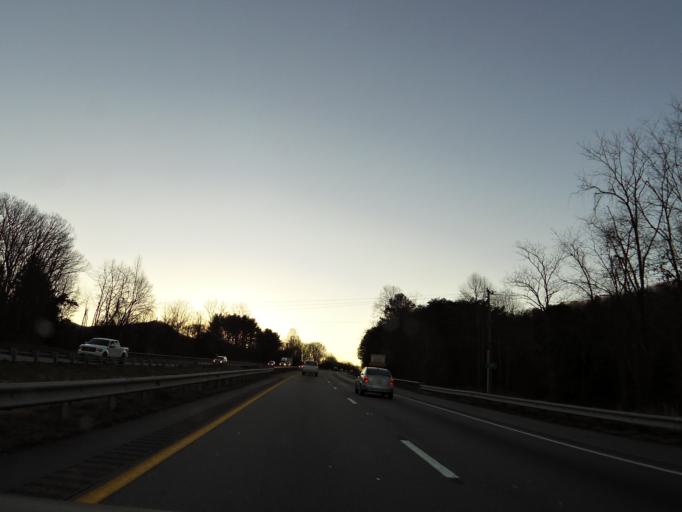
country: US
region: North Carolina
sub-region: Haywood County
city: Canton
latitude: 35.5510
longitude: -82.7324
